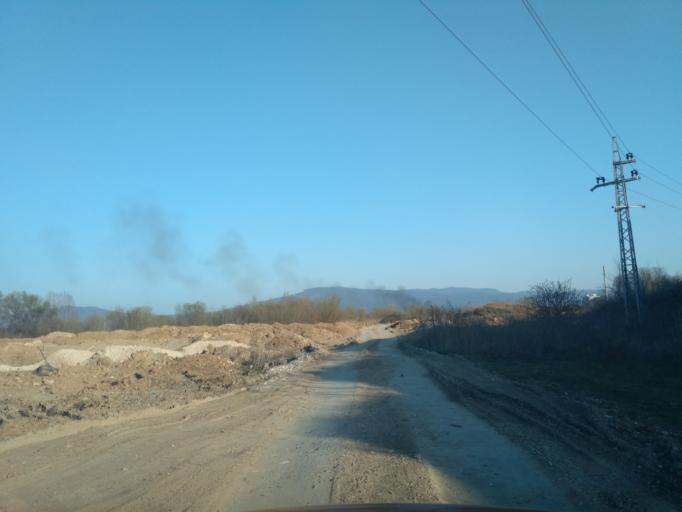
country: SK
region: Kosicky
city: Kosice
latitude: 48.6694
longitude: 21.3013
